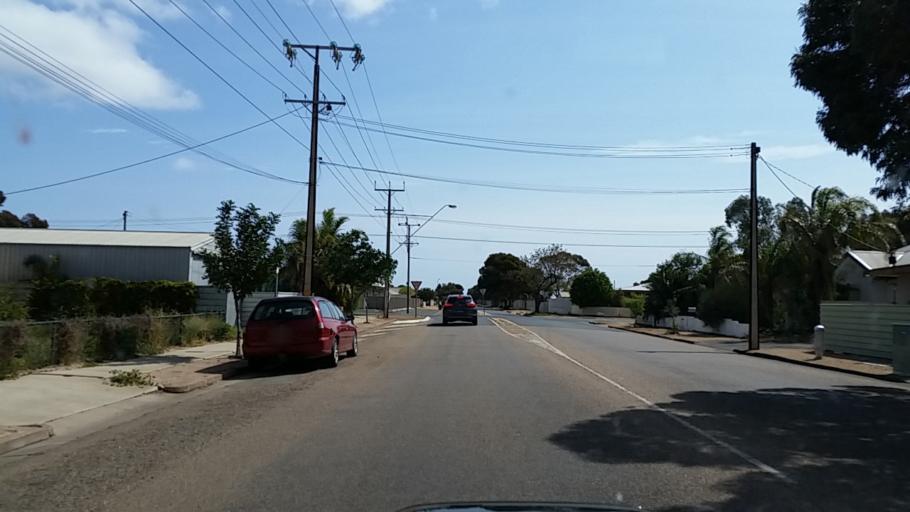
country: AU
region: South Australia
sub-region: Port Pirie City and Dists
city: Port Pirie
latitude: -33.1894
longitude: 137.9983
